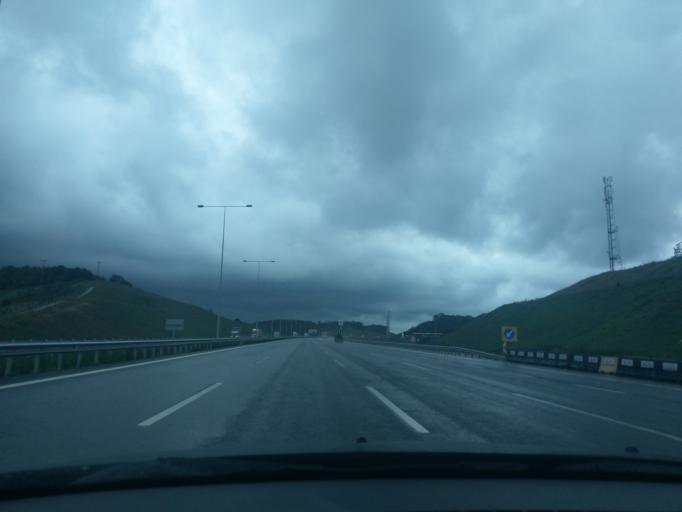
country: TR
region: Istanbul
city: Kemerburgaz
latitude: 41.2341
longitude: 28.8797
